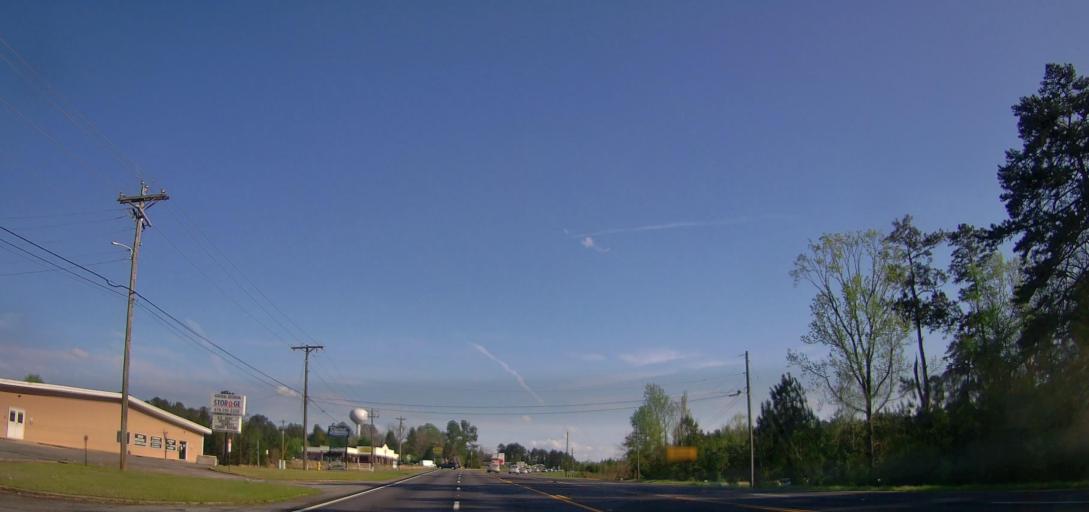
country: US
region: Georgia
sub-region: Baldwin County
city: Milledgeville
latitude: 33.1738
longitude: -83.2832
